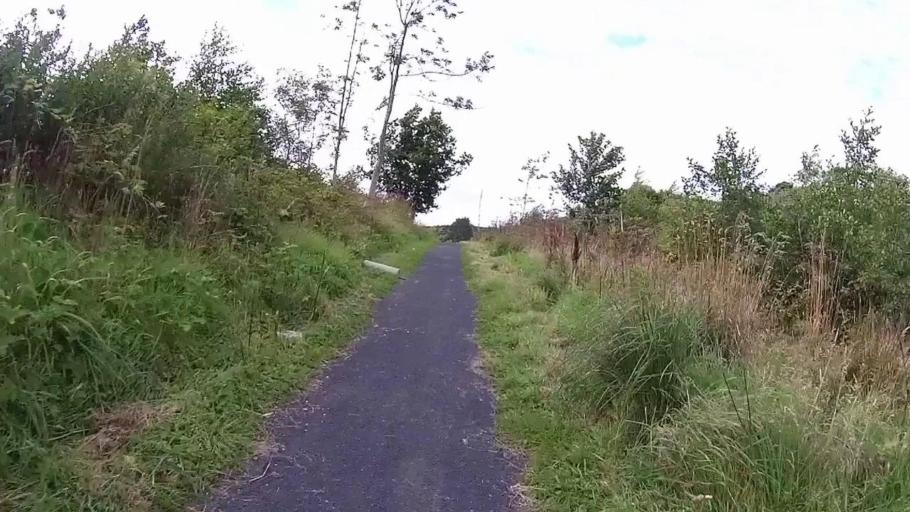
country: GB
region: Scotland
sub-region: Fife
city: Glenrothes
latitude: 56.2195
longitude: -3.1720
